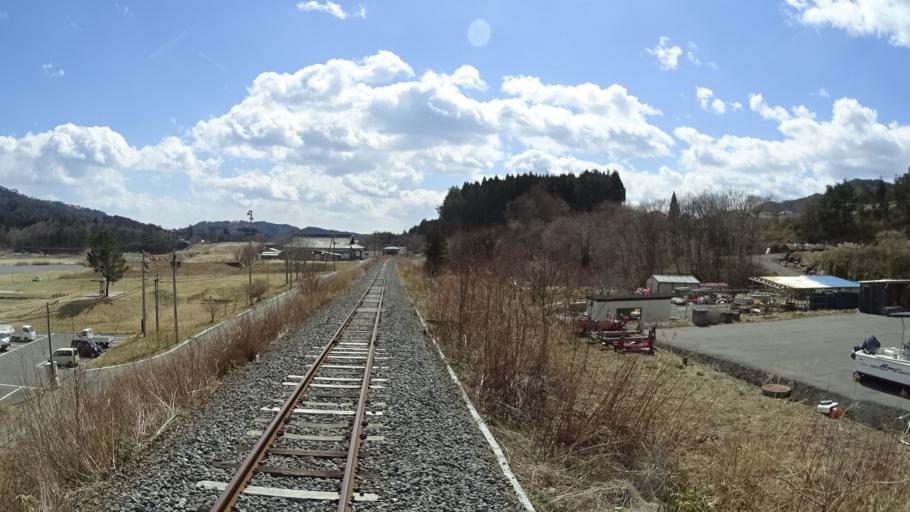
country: JP
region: Iwate
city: Yamada
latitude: 39.4367
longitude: 141.9748
